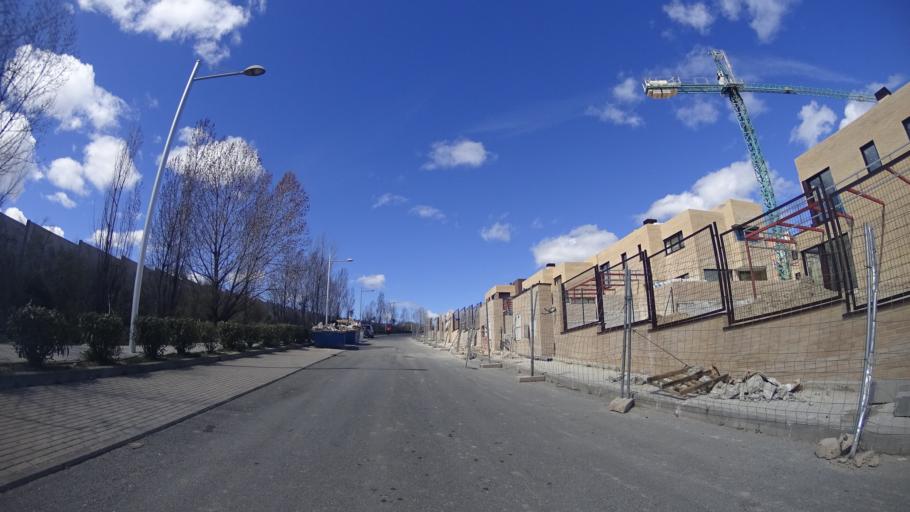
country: ES
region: Madrid
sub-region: Provincia de Madrid
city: Torrelodones
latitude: 40.5631
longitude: -3.9210
